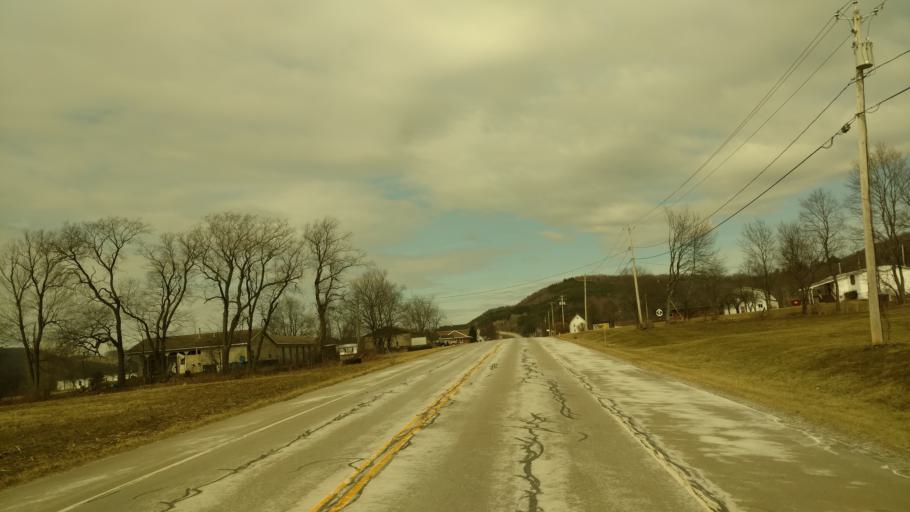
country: US
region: New York
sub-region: Allegany County
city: Wellsville
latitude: 42.0462
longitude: -77.9159
